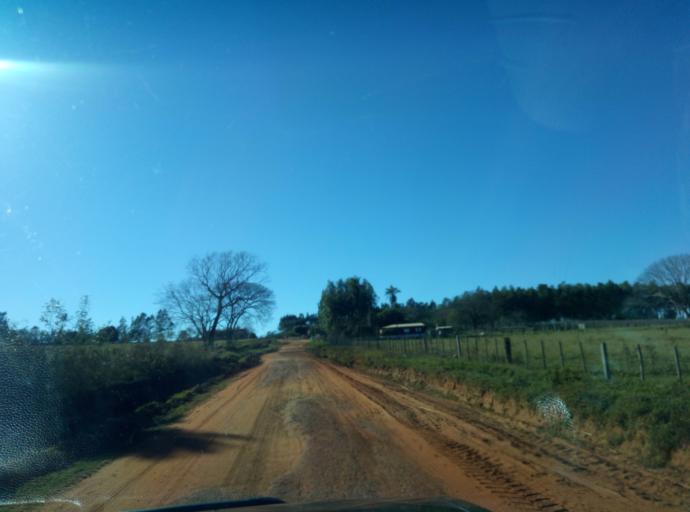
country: PY
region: Caaguazu
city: Doctor Cecilio Baez
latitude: -25.1641
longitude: -56.2542
